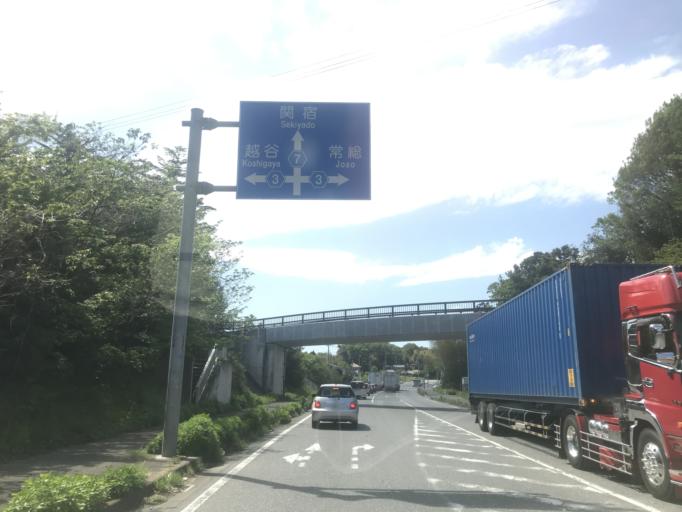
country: JP
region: Chiba
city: Noda
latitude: 35.9696
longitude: 139.8856
